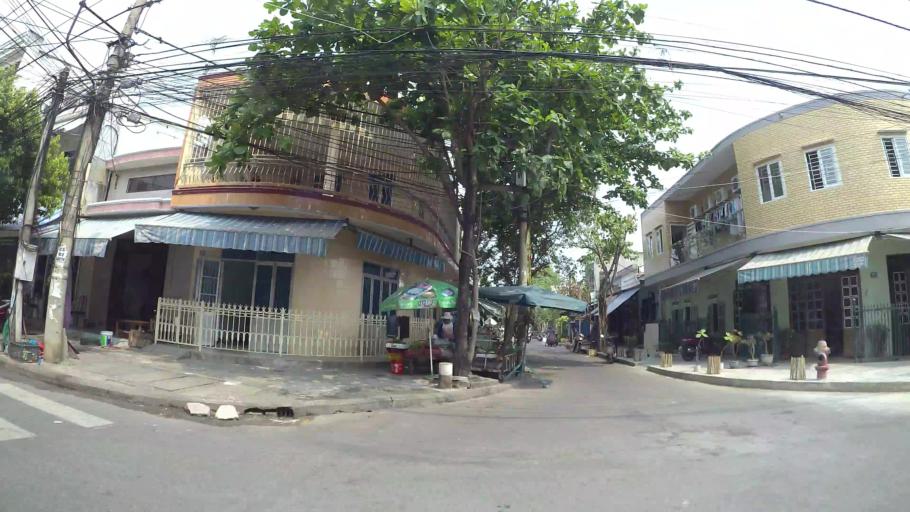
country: VN
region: Da Nang
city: Da Nang
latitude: 16.0849
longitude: 108.2300
